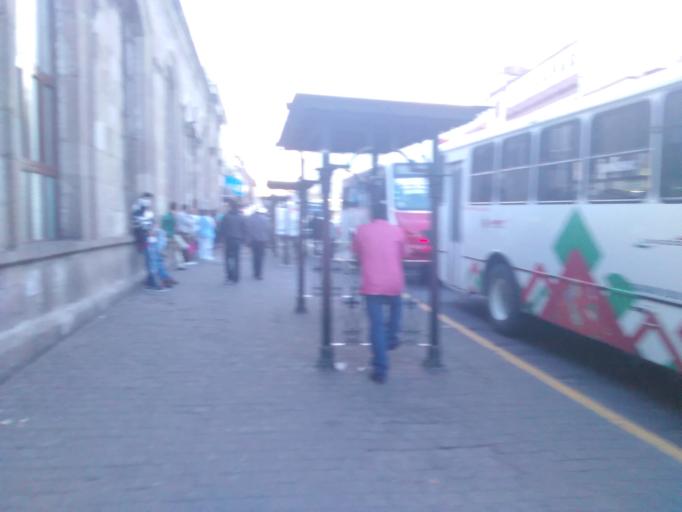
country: MX
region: Nayarit
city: Tepic
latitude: 21.5127
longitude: -104.8931
